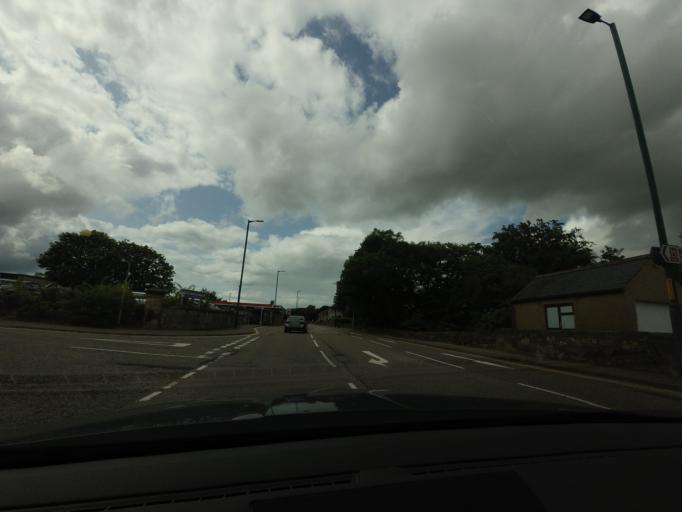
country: GB
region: Scotland
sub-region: Moray
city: Elgin
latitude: 57.6467
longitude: -3.3300
